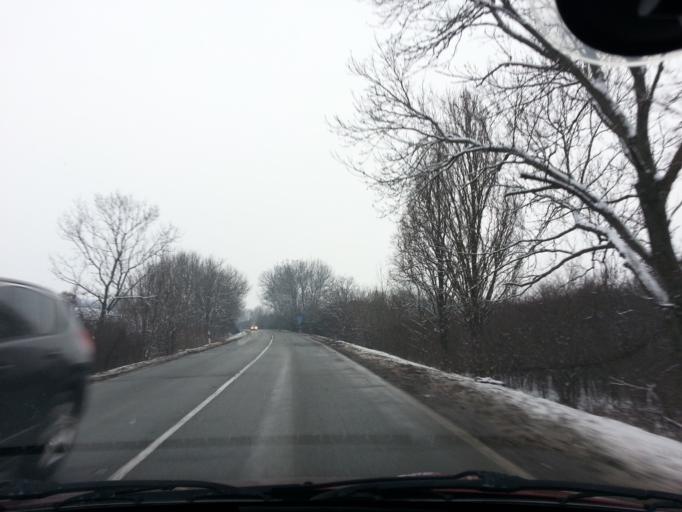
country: HU
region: Nograd
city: Szurdokpuspoki
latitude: 47.8792
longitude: 19.6719
